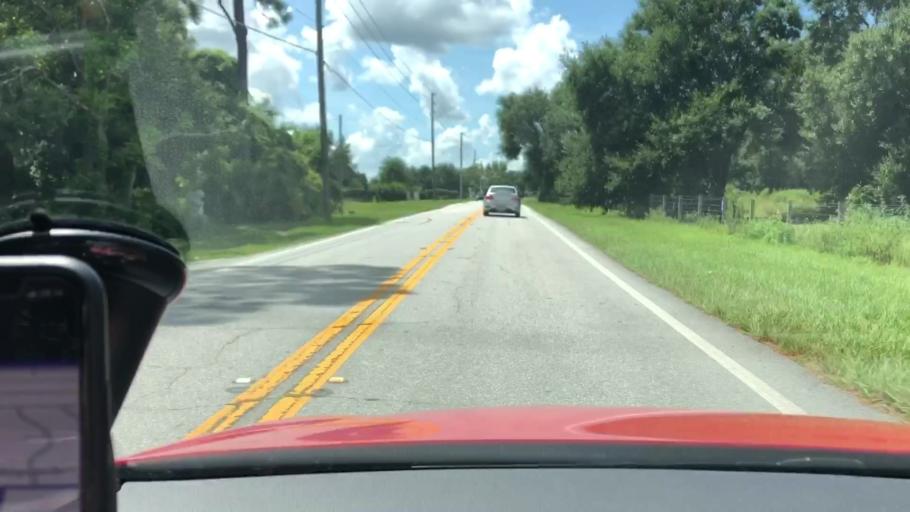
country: US
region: Florida
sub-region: Lake County
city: Eustis
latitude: 28.8362
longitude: -81.6545
